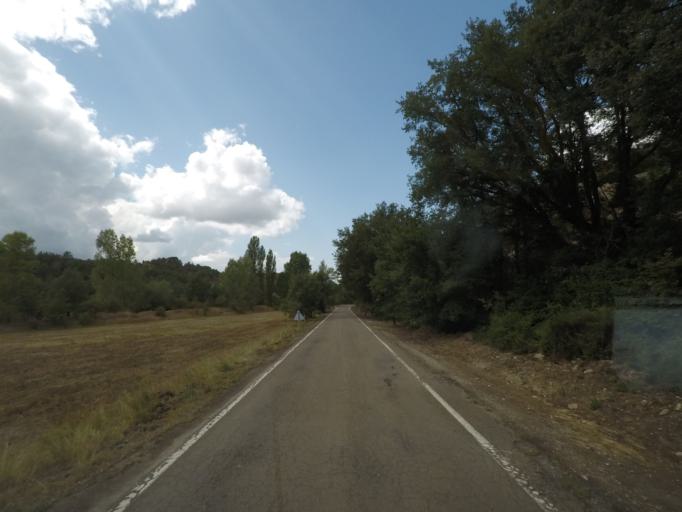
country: ES
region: Aragon
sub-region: Provincia de Huesca
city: Yebra de Basa
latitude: 42.3904
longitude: -0.2838
